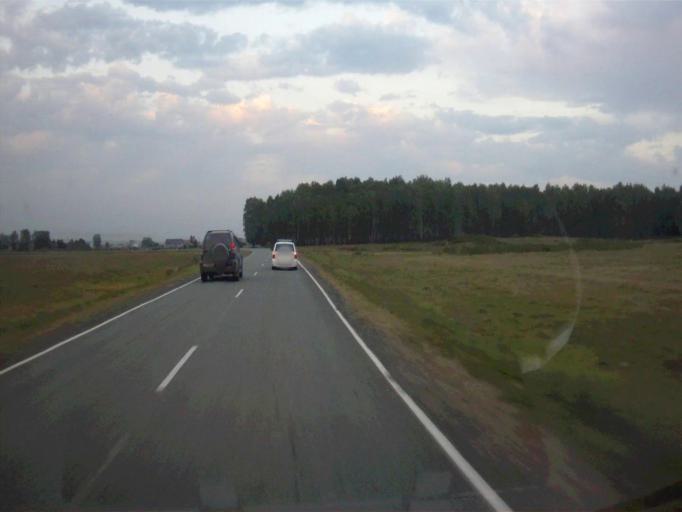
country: RU
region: Chelyabinsk
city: Chebarkul'
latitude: 55.1782
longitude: 60.4702
